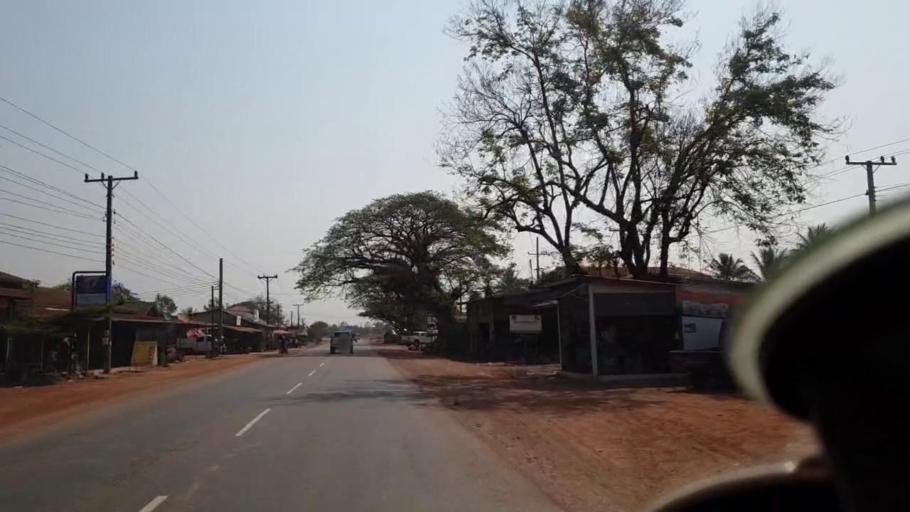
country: TH
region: Nong Khai
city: Phon Phisai
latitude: 18.0472
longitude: 102.8775
